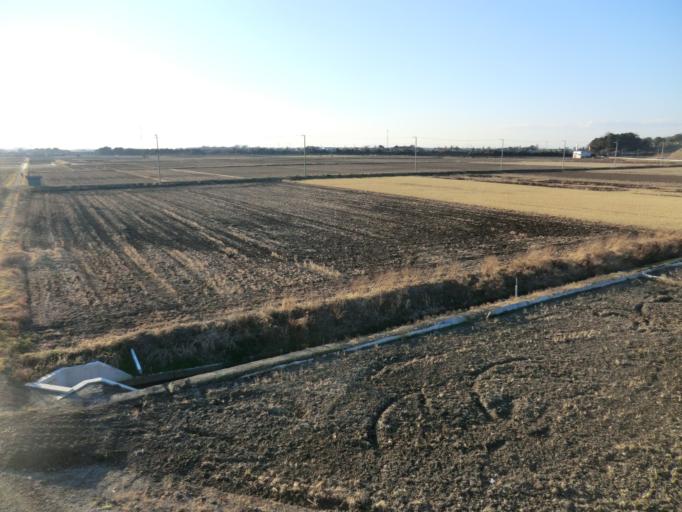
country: JP
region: Ibaraki
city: Mitsukaido
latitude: 35.9886
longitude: 140.0348
